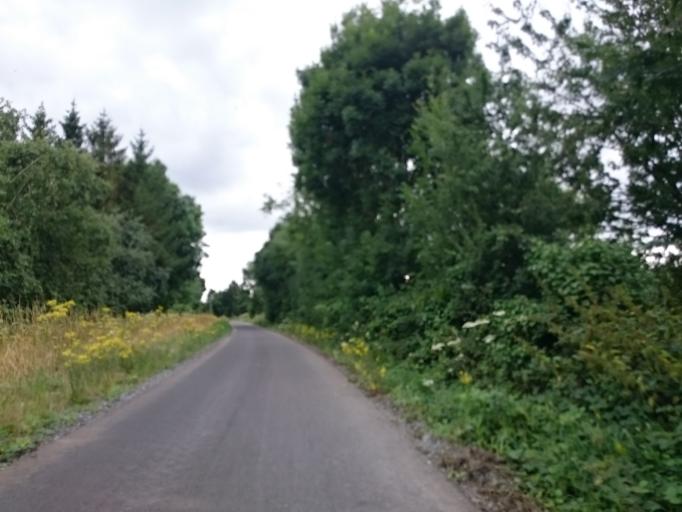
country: FR
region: Lower Normandy
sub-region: Departement du Calvados
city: Bully
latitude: 49.0968
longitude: -0.4091
